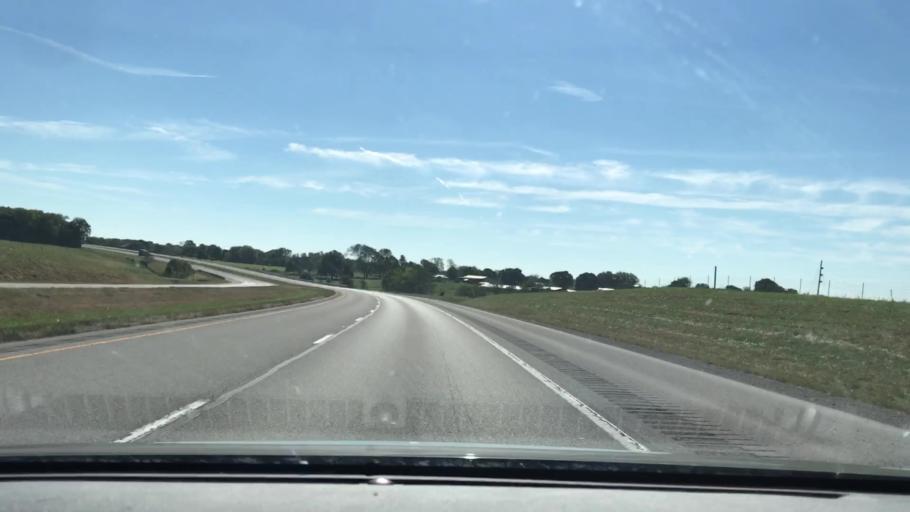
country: US
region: Kentucky
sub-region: Todd County
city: Elkton
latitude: 36.8128
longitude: -87.1389
